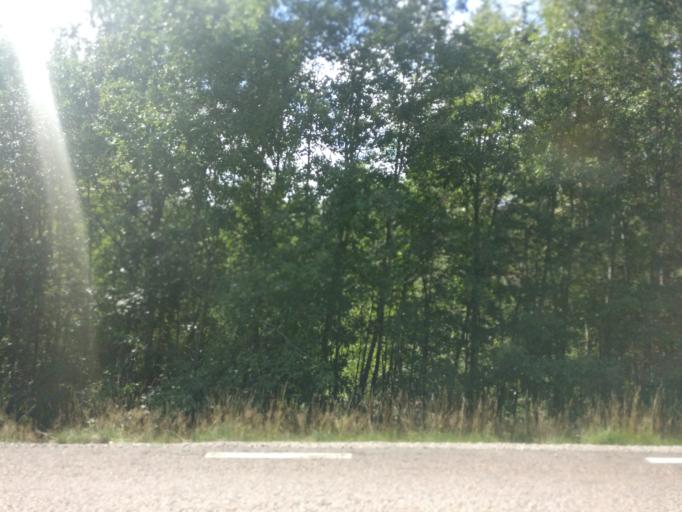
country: SE
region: Vaermland
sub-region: Hagfors Kommun
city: Ekshaerad
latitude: 60.2832
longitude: 13.4039
